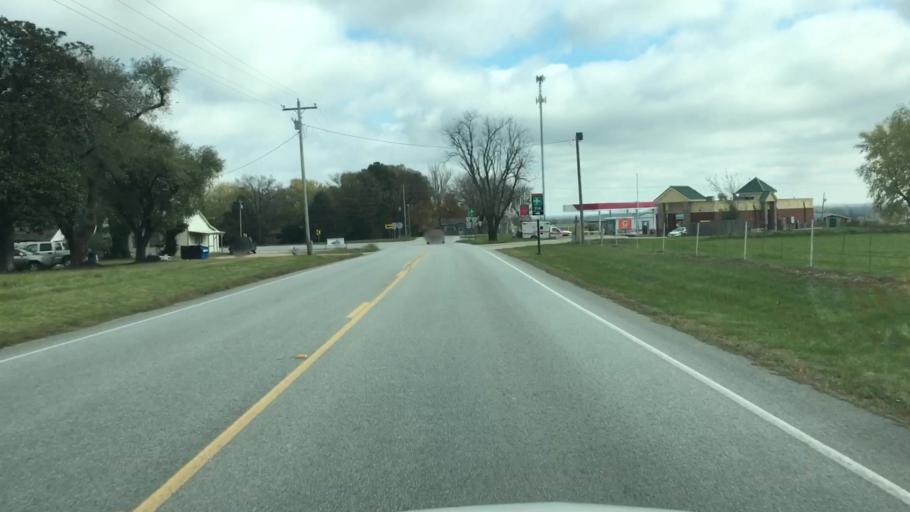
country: US
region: Arkansas
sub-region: Benton County
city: Centerton
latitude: 36.2616
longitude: -94.3527
